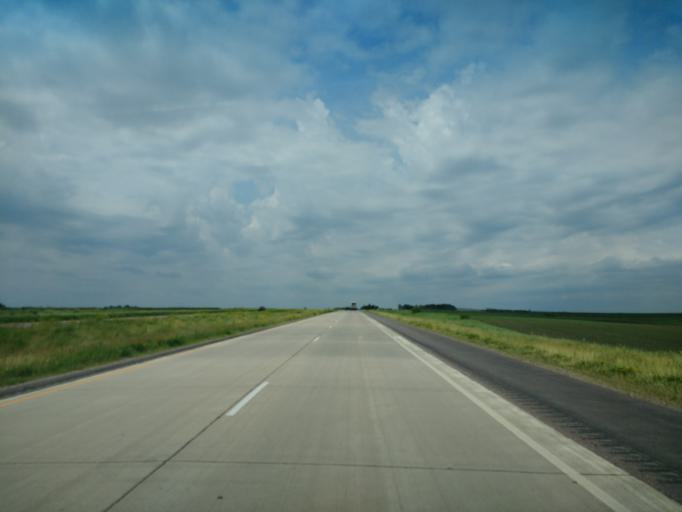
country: US
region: Minnesota
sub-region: Cottonwood County
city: Mountain Lake
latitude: 43.9493
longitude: -94.8062
